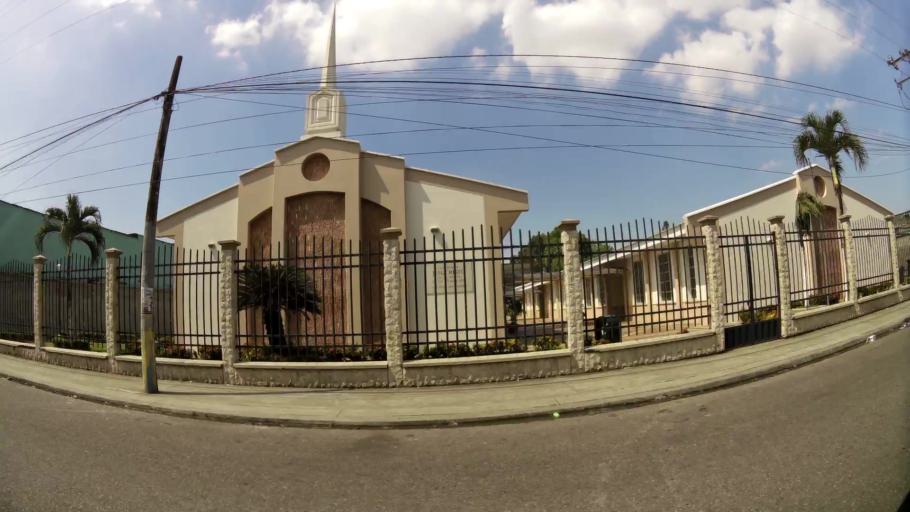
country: EC
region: Guayas
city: Guayaquil
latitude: -2.1212
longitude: -79.9280
